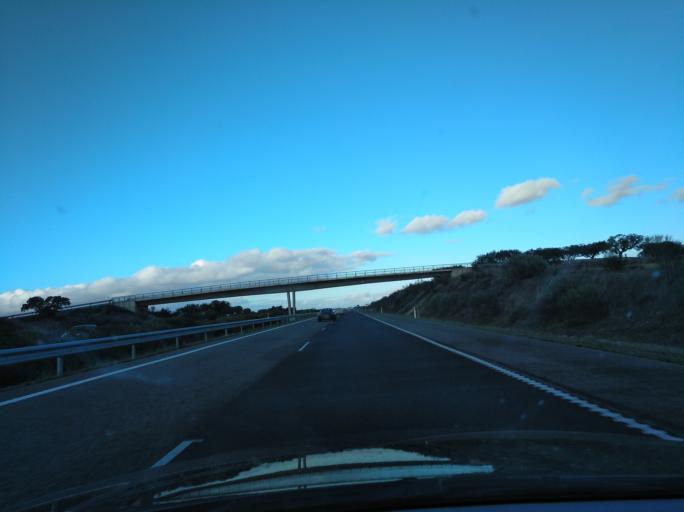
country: PT
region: Beja
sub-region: Ourique
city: Ourique
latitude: 37.5832
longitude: -8.1834
